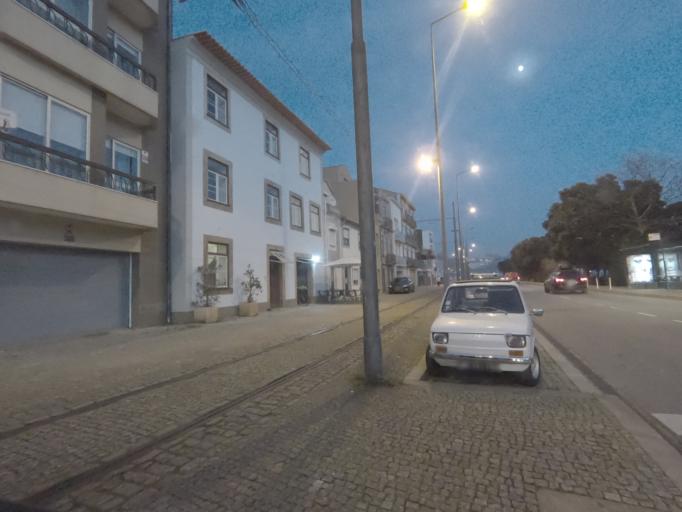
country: PT
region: Porto
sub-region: Vila Nova de Gaia
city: Canidelo
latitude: 41.1471
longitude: -8.6600
